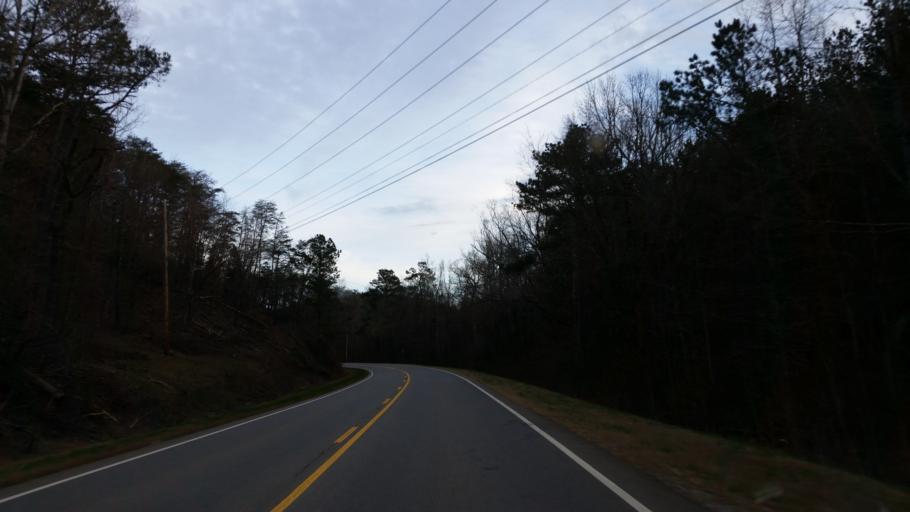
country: US
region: Georgia
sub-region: Bartow County
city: Rydal
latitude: 34.4486
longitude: -84.7550
